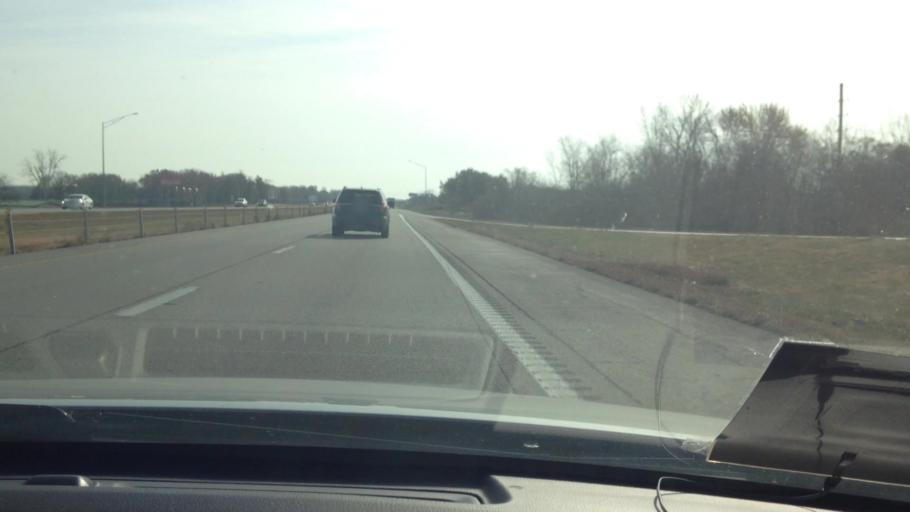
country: US
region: Missouri
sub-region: Cass County
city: Peculiar
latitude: 38.7216
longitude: -94.4538
